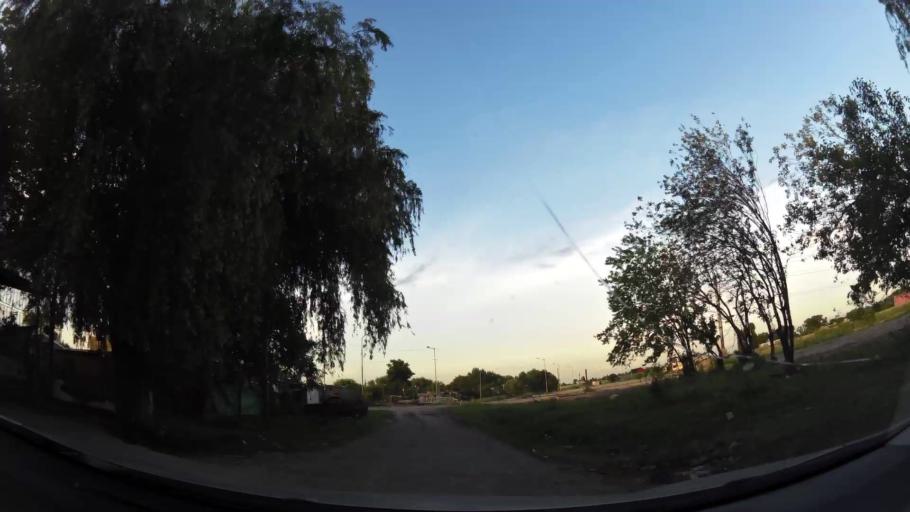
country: AR
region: Buenos Aires
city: Santa Catalina - Dique Lujan
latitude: -34.4412
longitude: -58.6601
